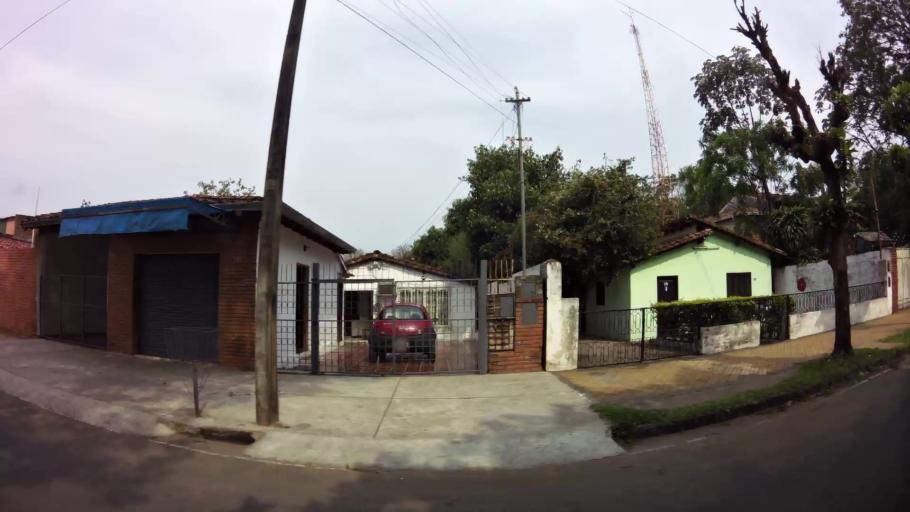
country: PY
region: Central
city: Fernando de la Mora
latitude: -25.2991
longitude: -57.5592
